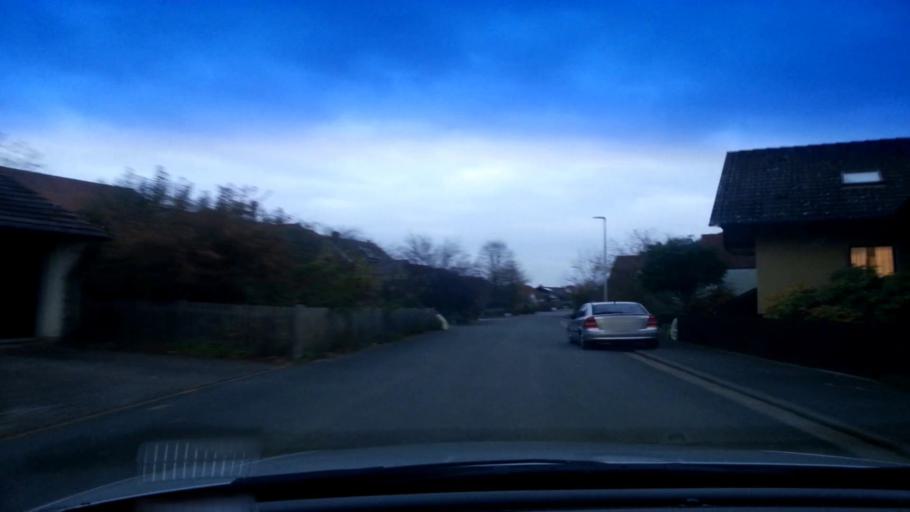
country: DE
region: Bavaria
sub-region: Upper Franconia
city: Kemmern
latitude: 49.9586
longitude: 10.8713
